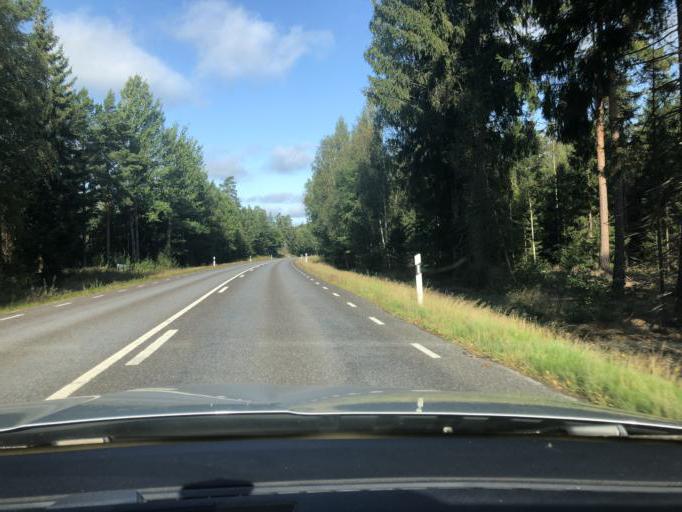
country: SE
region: Blekinge
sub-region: Karlshamns Kommun
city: Svangsta
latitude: 56.4966
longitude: 14.6920
